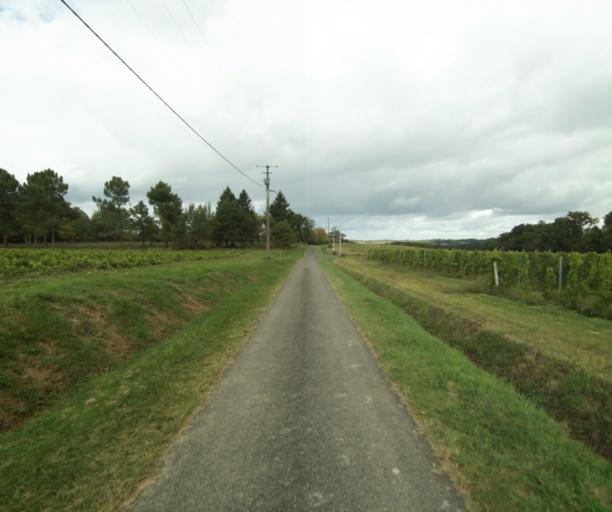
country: FR
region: Midi-Pyrenees
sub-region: Departement du Gers
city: Cazaubon
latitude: 43.8654
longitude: -0.0380
